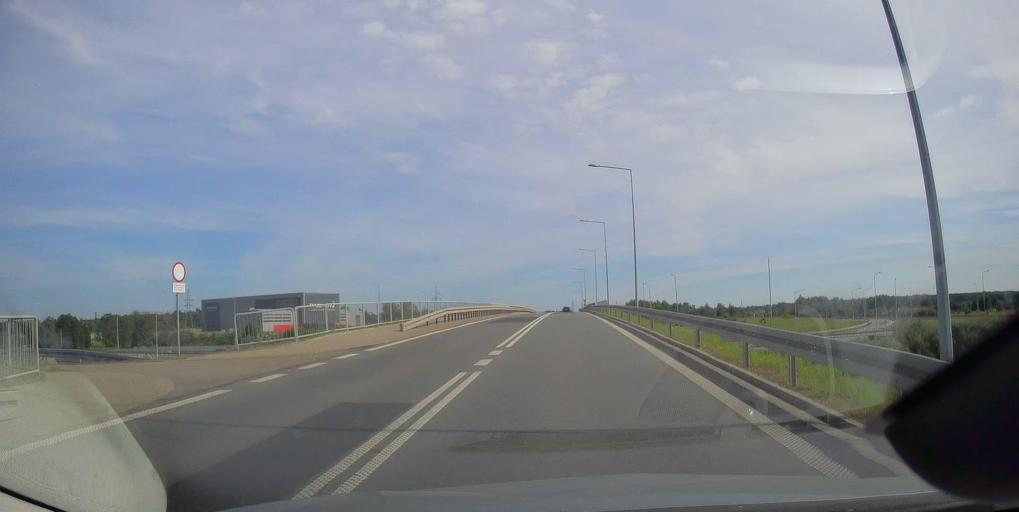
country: PL
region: Lodz Voivodeship
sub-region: Powiat tomaszowski
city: Tomaszow Mazowiecki
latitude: 51.5504
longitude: 19.9885
